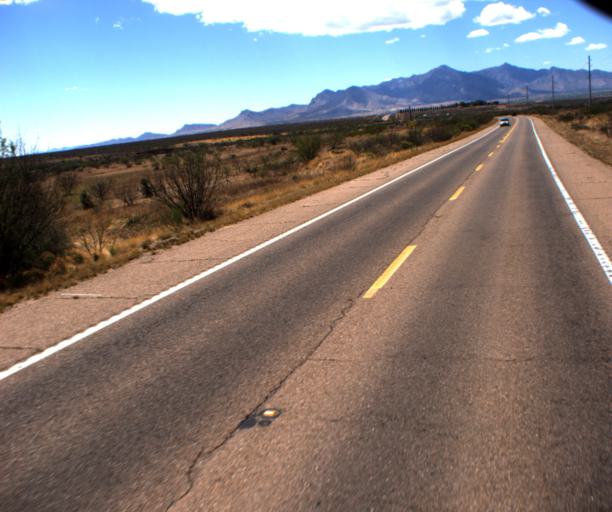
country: US
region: Arizona
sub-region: Cochise County
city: Naco
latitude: 31.3805
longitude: -110.0635
